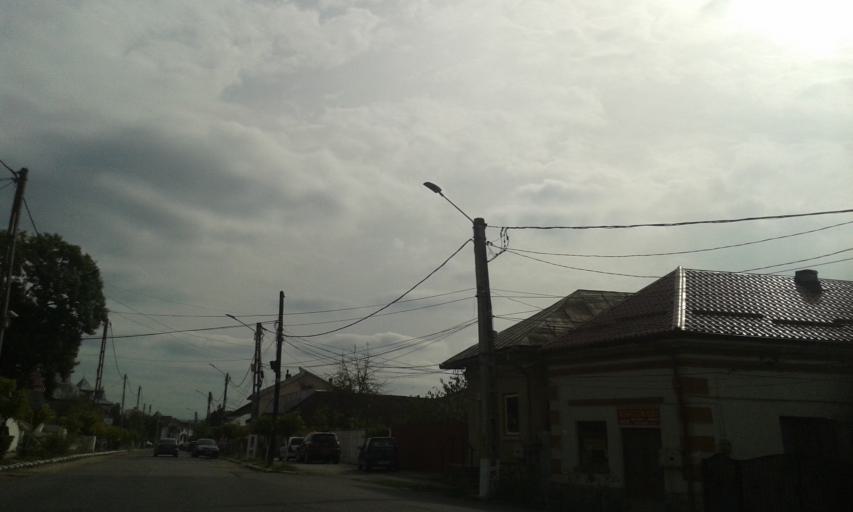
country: RO
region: Gorj
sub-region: Comuna Targu Carbunesti
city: Targu Carbunesti
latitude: 44.9575
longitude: 23.5117
